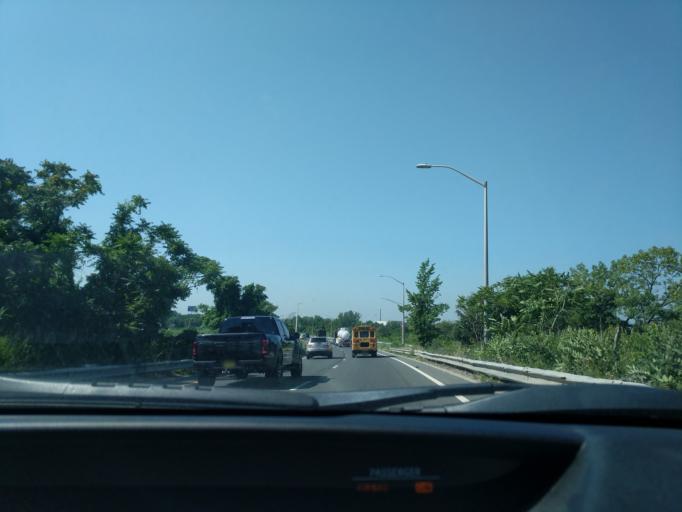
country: US
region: New York
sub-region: Richmond County
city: Bloomfield
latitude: 40.6199
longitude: -74.1766
